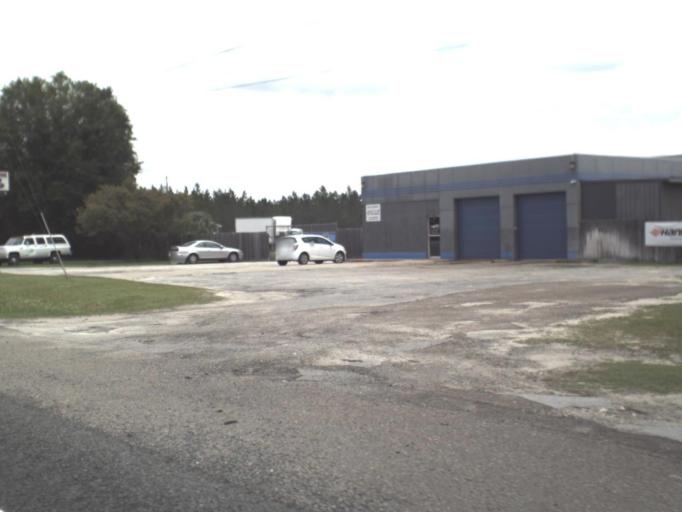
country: US
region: Florida
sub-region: Nassau County
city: Hilliard
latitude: 30.6677
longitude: -81.8917
